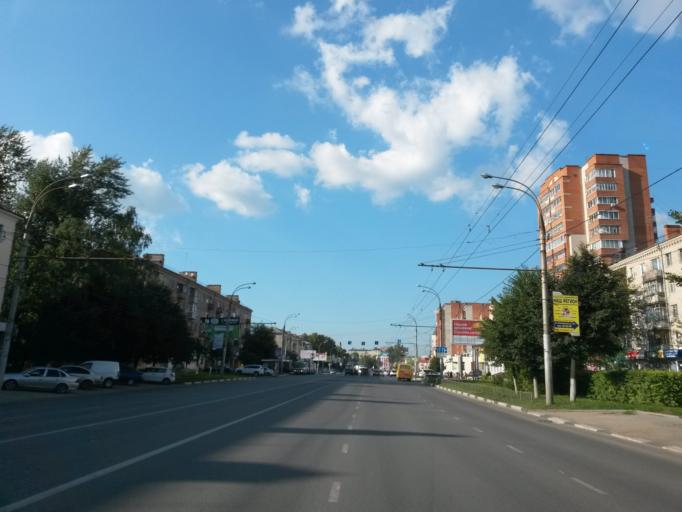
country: RU
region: Ivanovo
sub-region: Gorod Ivanovo
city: Ivanovo
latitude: 56.9701
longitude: 40.9736
